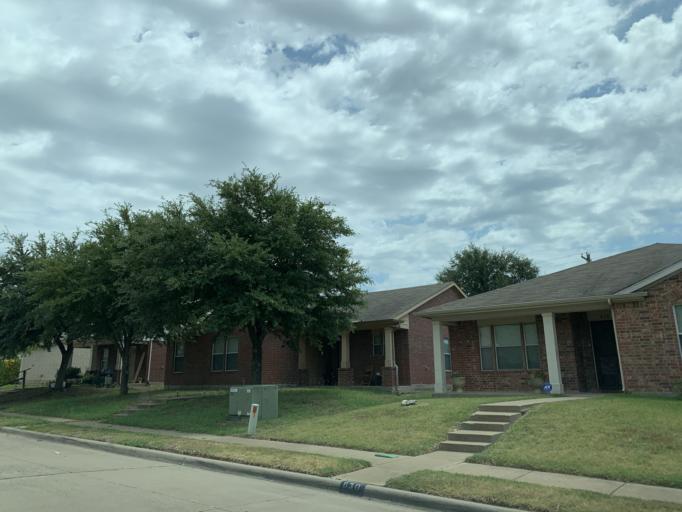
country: US
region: Texas
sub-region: Dallas County
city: DeSoto
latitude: 32.6552
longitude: -96.8114
